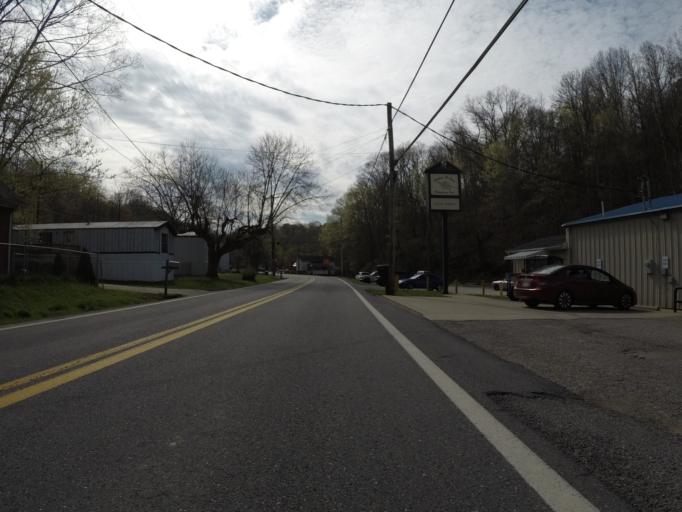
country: US
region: West Virginia
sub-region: Cabell County
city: Pea Ridge
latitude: 38.3769
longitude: -82.3726
